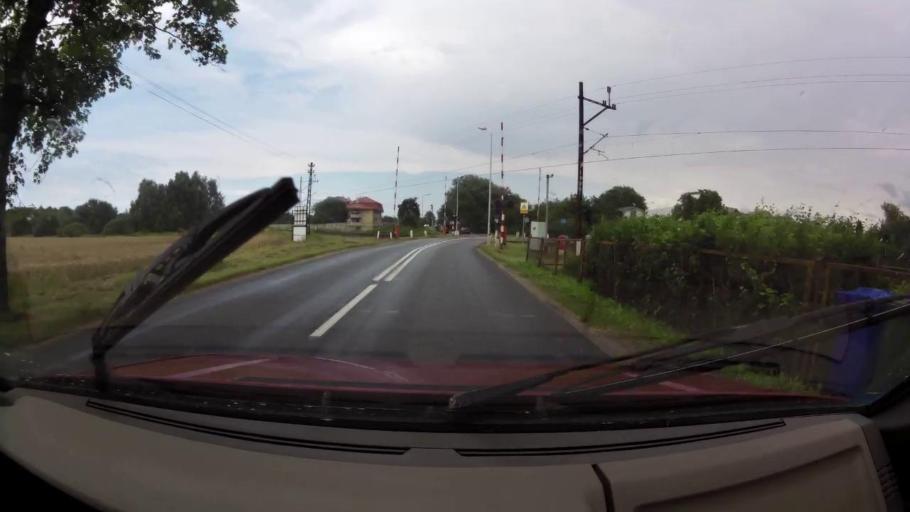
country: PL
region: West Pomeranian Voivodeship
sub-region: Koszalin
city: Koszalin
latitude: 54.1770
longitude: 16.1652
